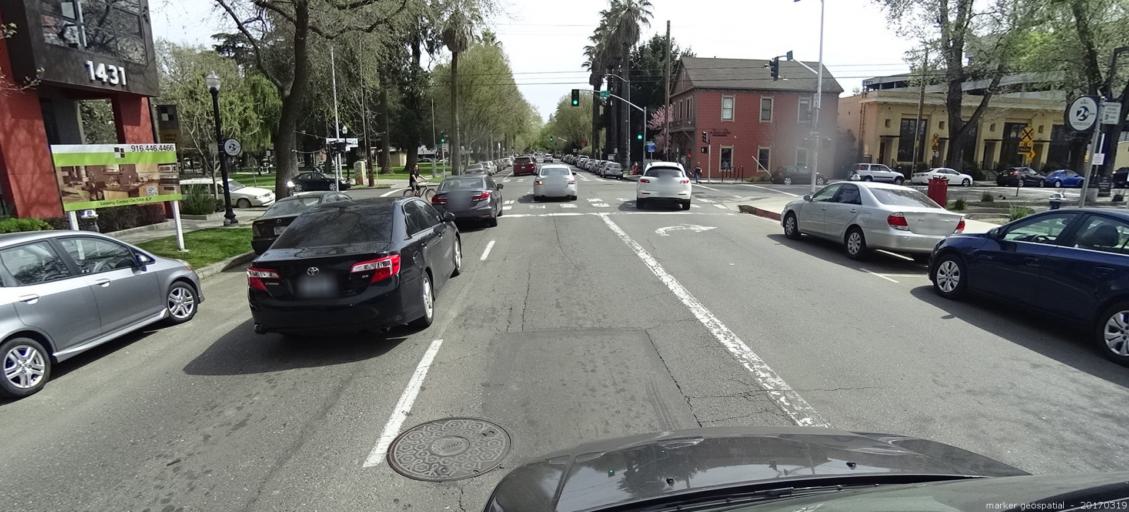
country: US
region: California
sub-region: Sacramento County
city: Sacramento
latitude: 38.5709
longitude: -121.4903
